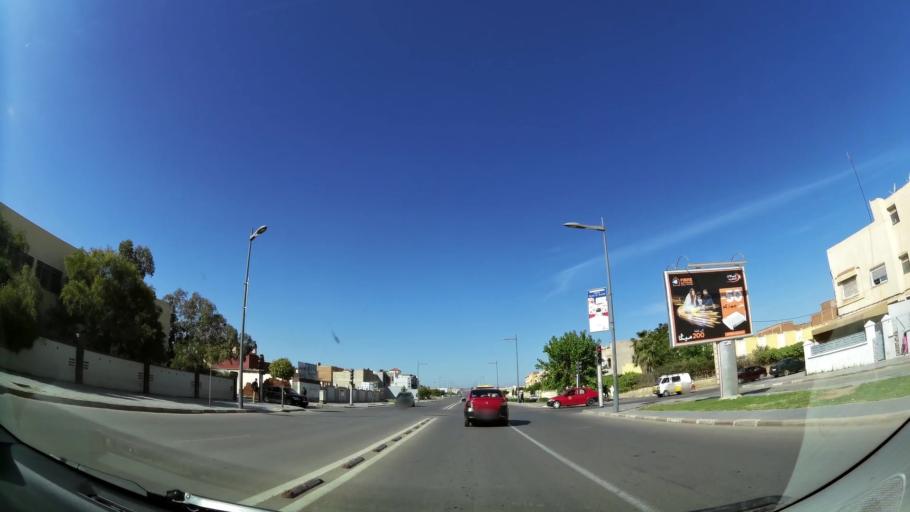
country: MA
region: Oriental
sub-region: Oujda-Angad
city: Oujda
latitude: 34.6700
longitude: -1.9373
